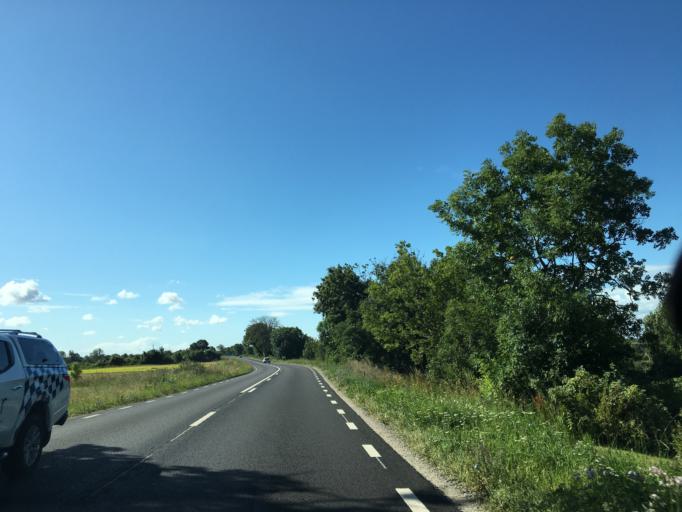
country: SE
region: Kalmar
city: Faerjestaden
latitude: 56.6616
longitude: 16.5186
